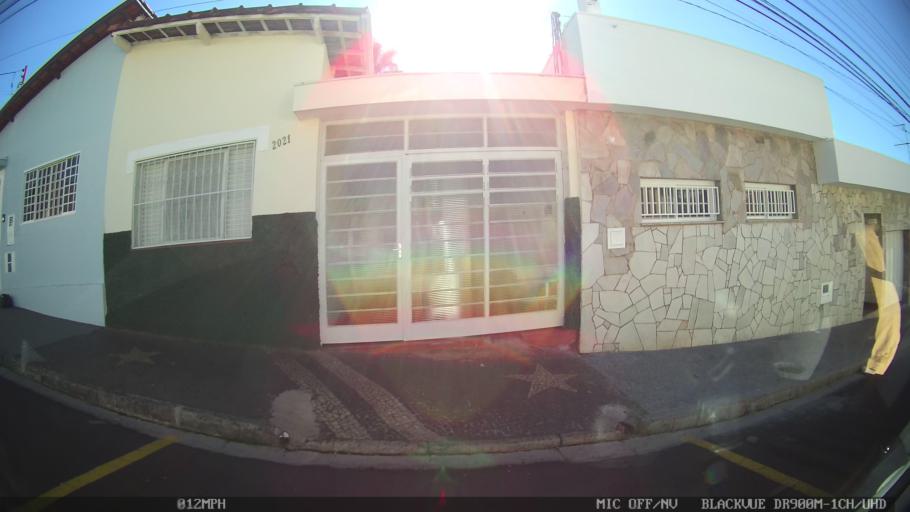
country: BR
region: Sao Paulo
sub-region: Franca
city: Franca
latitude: -20.5434
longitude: -47.3974
